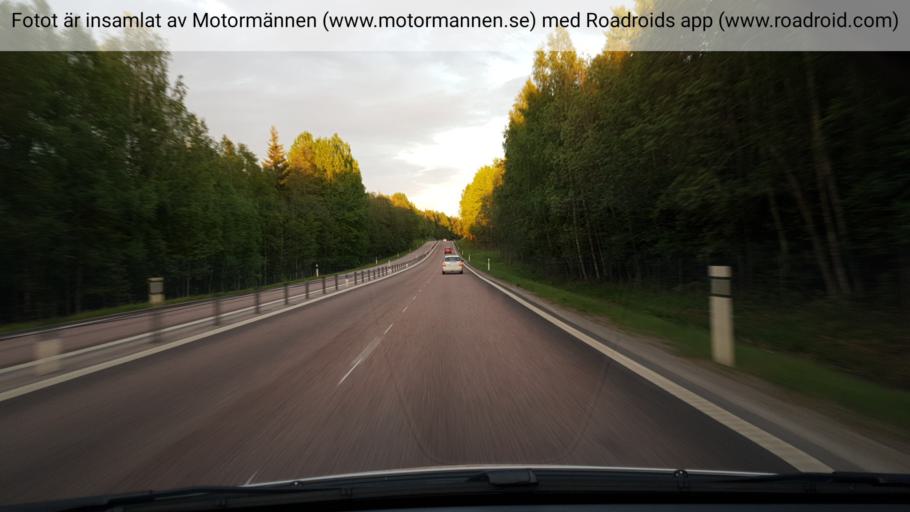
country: SE
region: Vaestmanland
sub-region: Norbergs Kommun
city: Norberg
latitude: 59.9381
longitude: 15.9066
